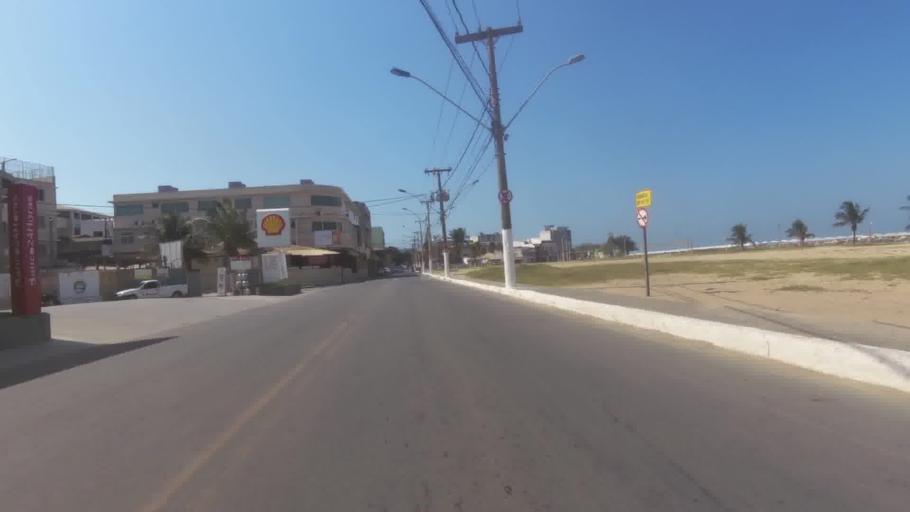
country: BR
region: Espirito Santo
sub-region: Marataizes
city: Marataizes
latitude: -21.0443
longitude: -40.8276
